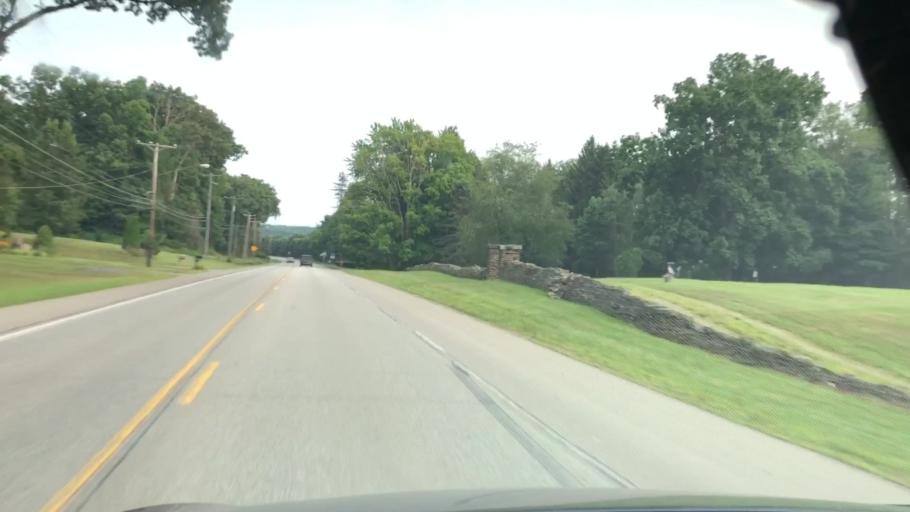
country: US
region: Pennsylvania
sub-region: Crawford County
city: Titusville
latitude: 41.6439
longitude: -79.7140
